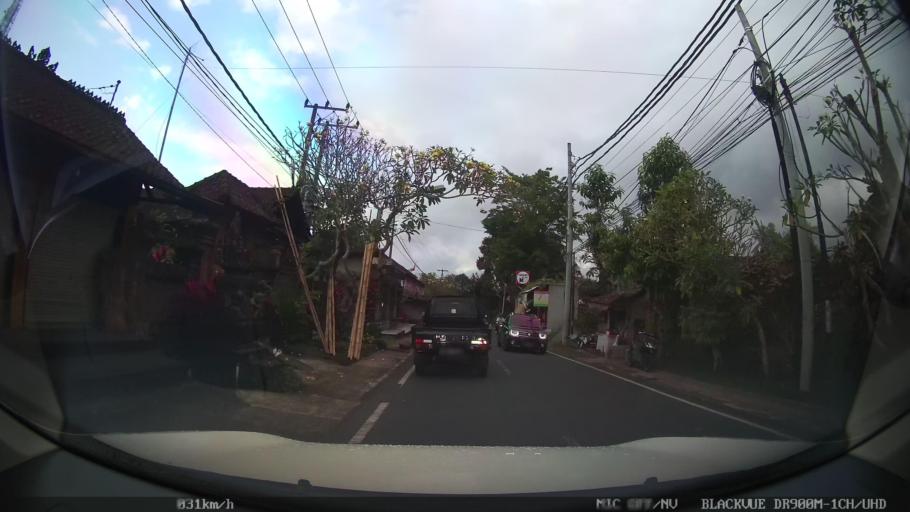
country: ID
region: Bali
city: Bunutan
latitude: -8.4749
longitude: 115.2495
